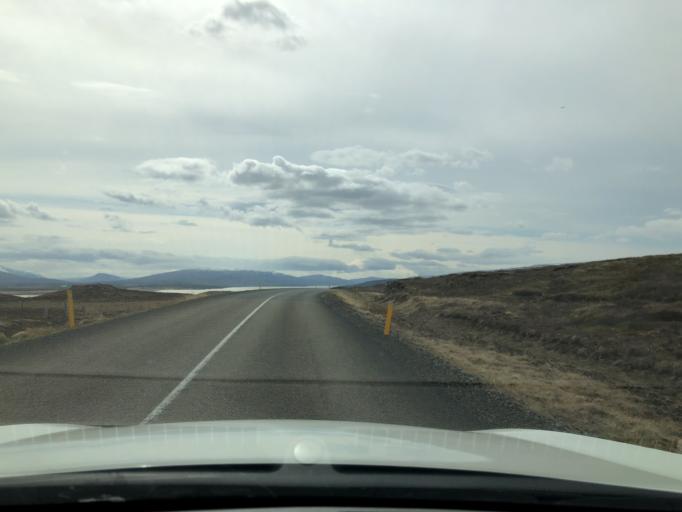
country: IS
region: East
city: Egilsstadir
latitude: 65.2471
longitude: -14.5115
